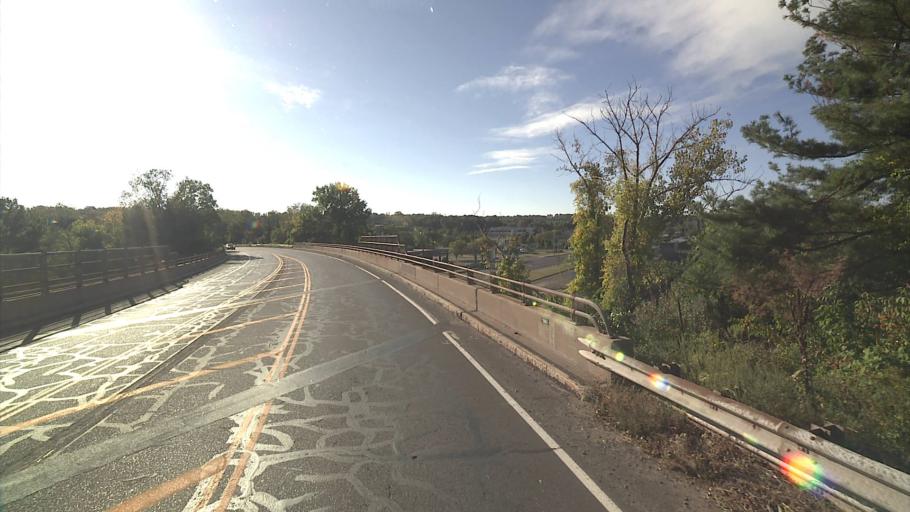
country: US
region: Connecticut
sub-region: New Haven County
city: Wallingford
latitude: 41.4863
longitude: -72.8103
